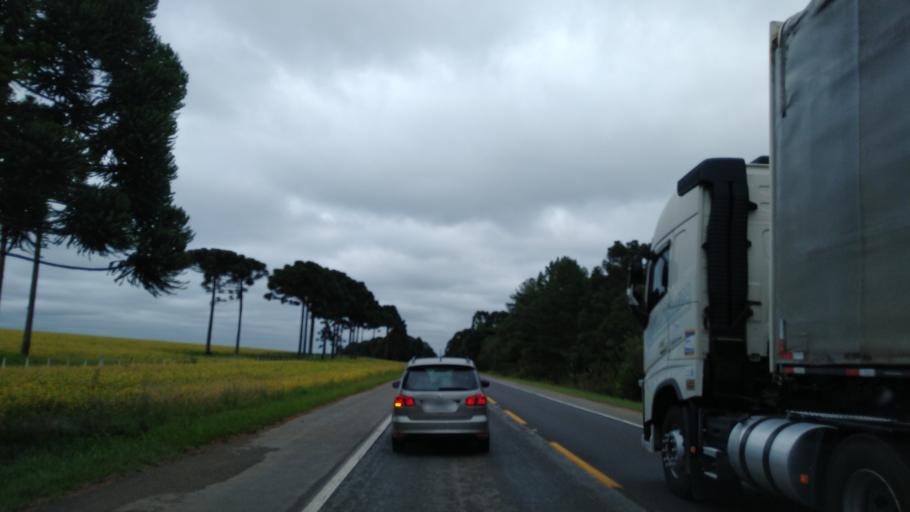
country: BR
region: Santa Catarina
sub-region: Tres Barras
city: Tres Barras
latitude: -26.1682
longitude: -50.1020
